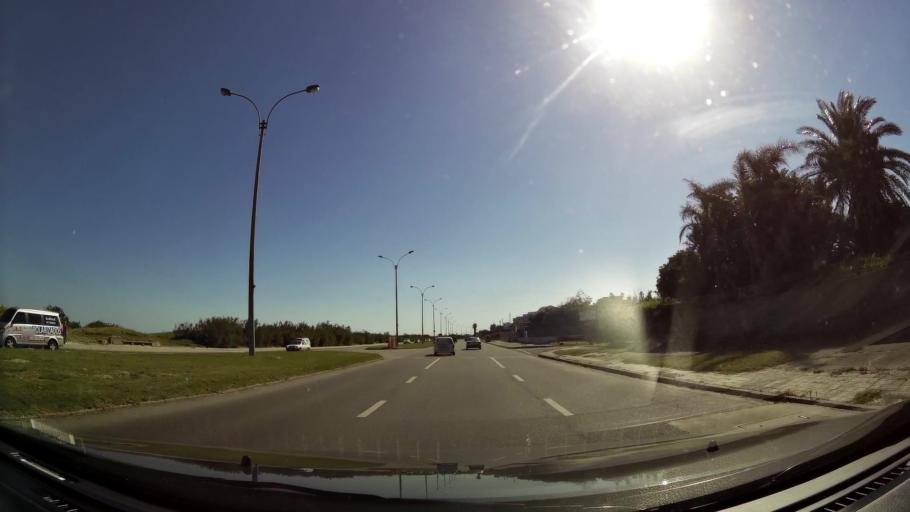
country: UY
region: Canelones
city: Barra de Carrasco
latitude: -34.8853
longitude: -56.0421
